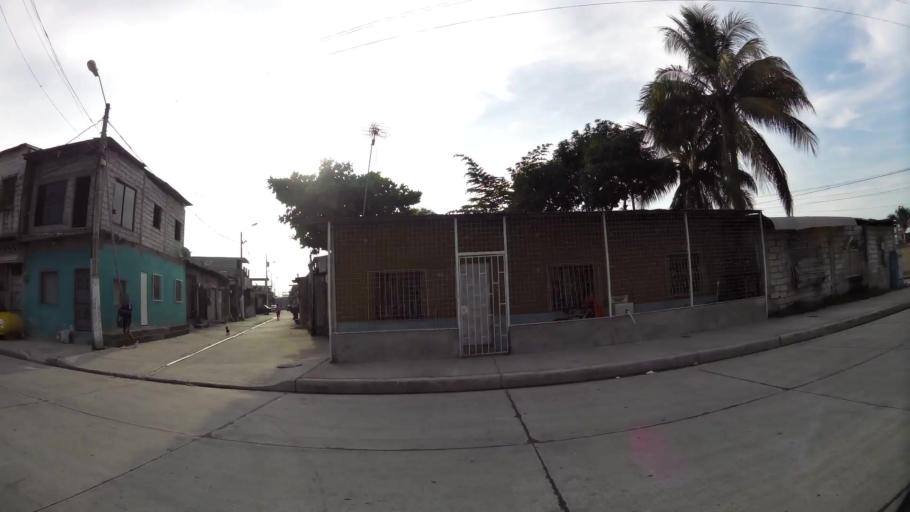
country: EC
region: Guayas
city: Eloy Alfaro
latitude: -2.0909
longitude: -79.8975
